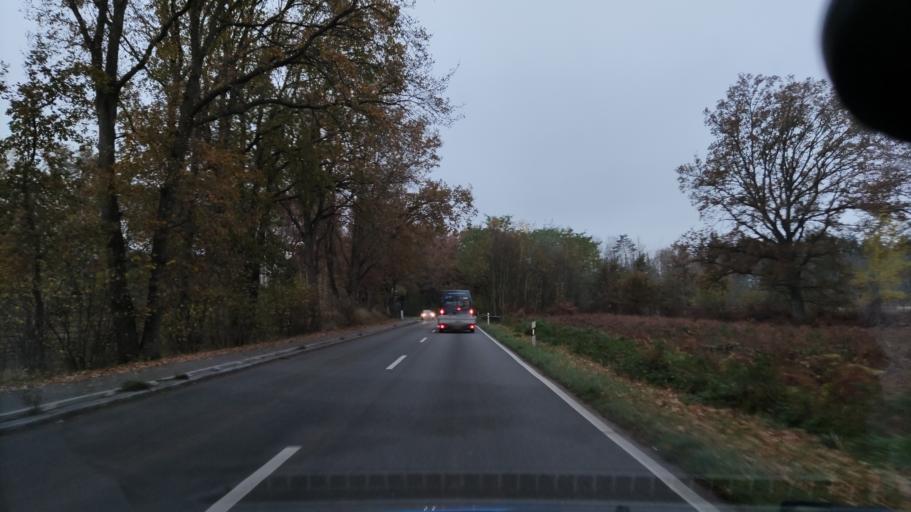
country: DE
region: Schleswig-Holstein
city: Gross Gronau
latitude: 53.8165
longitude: 10.7136
